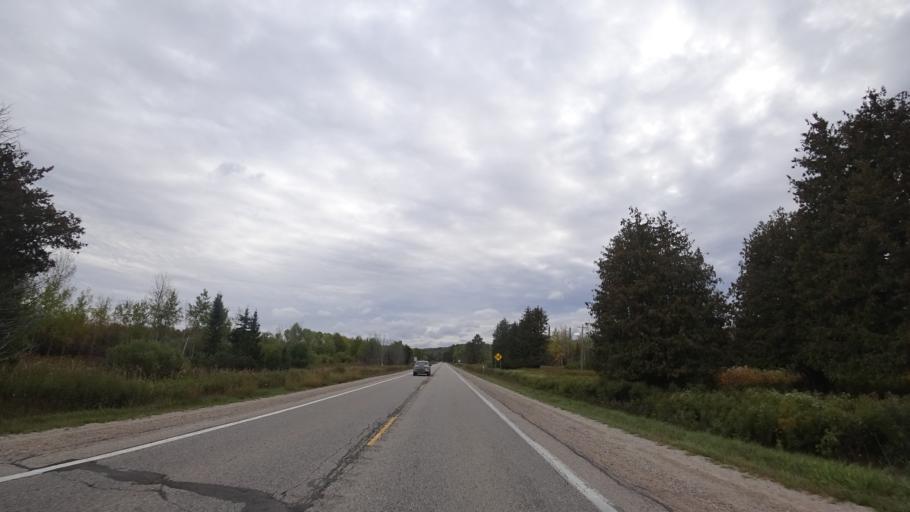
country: US
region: Michigan
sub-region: Charlevoix County
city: Boyne City
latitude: 45.2208
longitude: -84.9224
